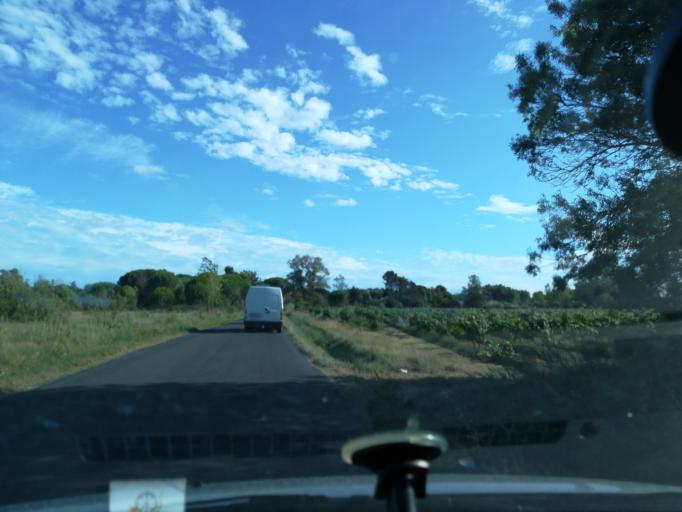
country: FR
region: Languedoc-Roussillon
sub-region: Departement de l'Herault
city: Vias
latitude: 43.2930
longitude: 3.3908
